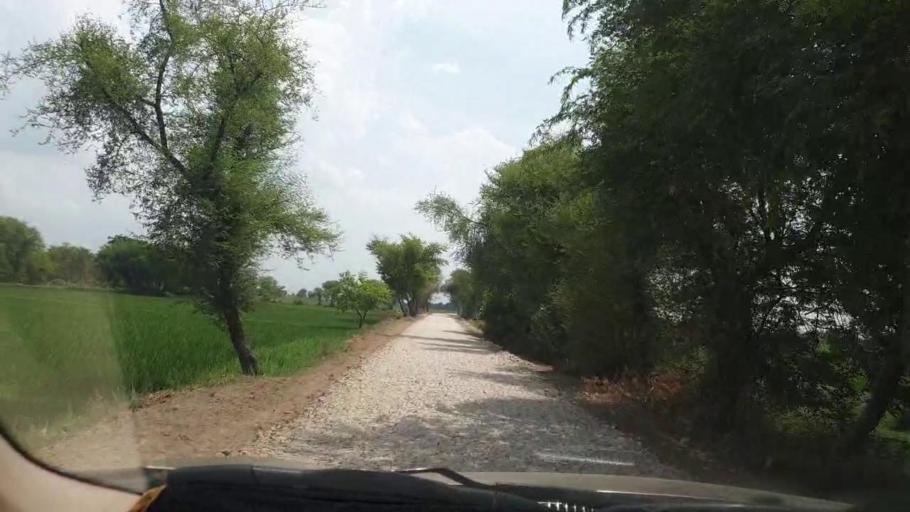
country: PK
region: Sindh
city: Larkana
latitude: 27.5703
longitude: 68.1100
